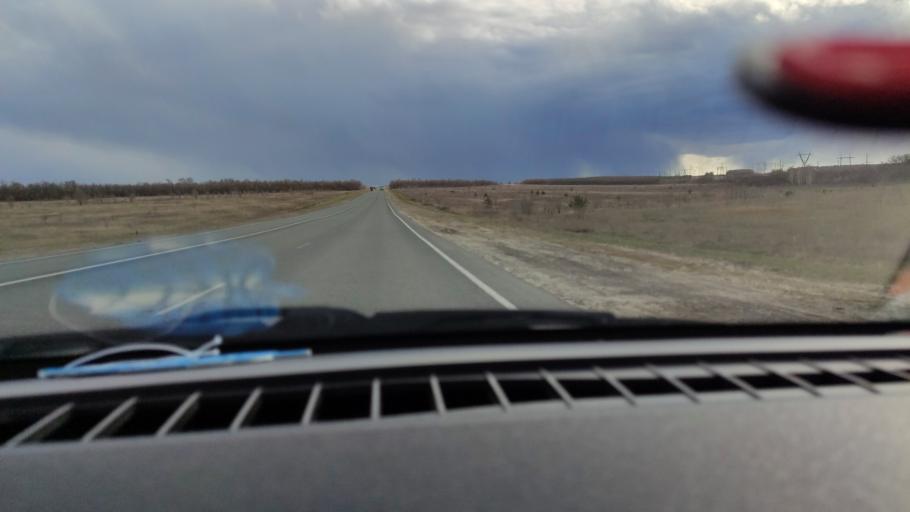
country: RU
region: Saratov
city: Sinodskoye
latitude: 51.9136
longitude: 46.5557
